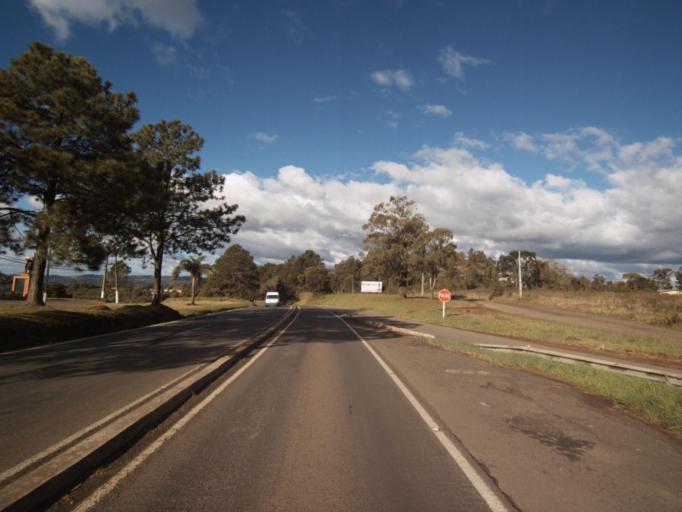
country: BR
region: Santa Catarina
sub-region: Joacaba
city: Joacaba
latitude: -27.1798
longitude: -51.5379
